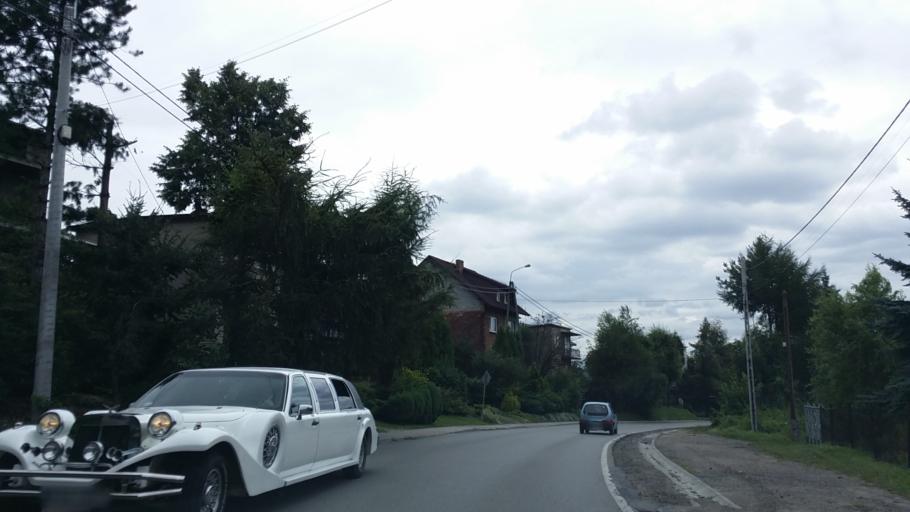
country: PL
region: Lesser Poland Voivodeship
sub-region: Powiat wadowicki
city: Tomice
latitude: 49.8908
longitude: 19.4738
